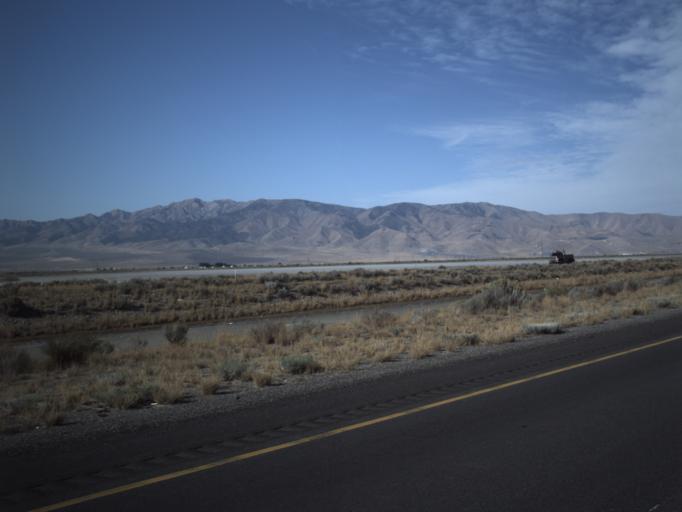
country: US
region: Utah
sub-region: Tooele County
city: Grantsville
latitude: 40.6772
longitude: -112.4063
